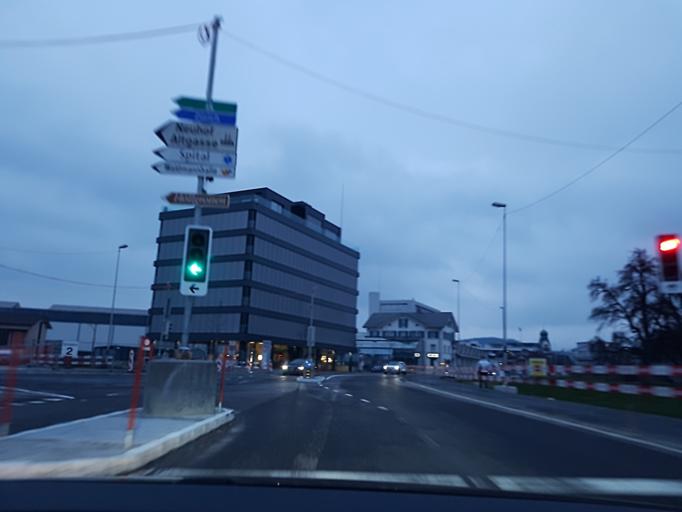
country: CH
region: Zug
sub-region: Zug
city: Baar
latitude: 47.1888
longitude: 8.5221
